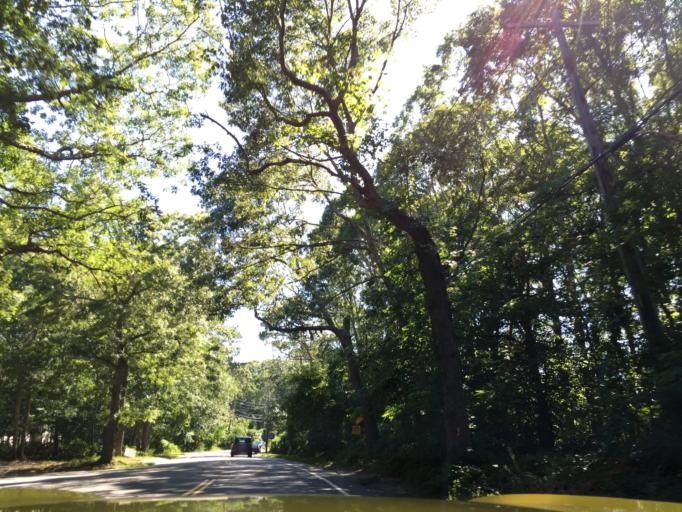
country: US
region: New York
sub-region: Suffolk County
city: North Sea
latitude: 40.9456
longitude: -72.3993
